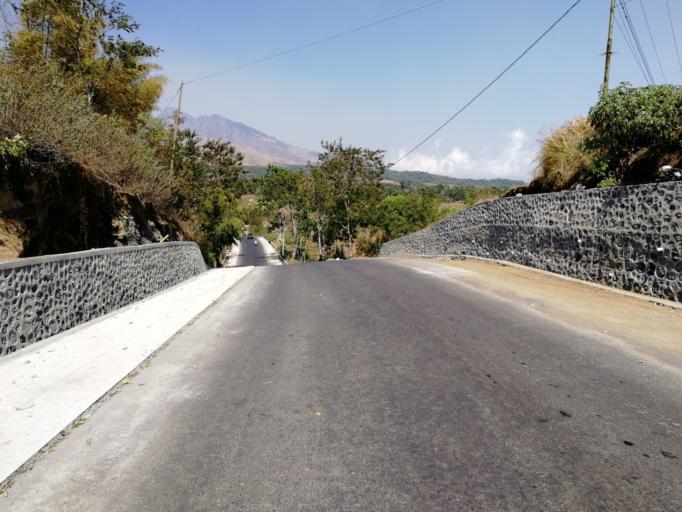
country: ID
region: West Nusa Tenggara
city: Sembalunlawang
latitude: -8.3575
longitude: 116.5157
